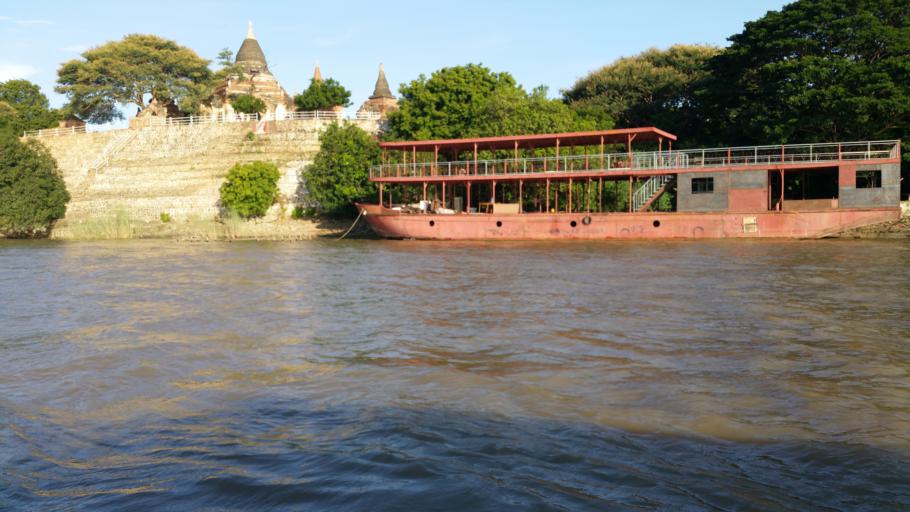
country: MM
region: Magway
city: Pakokku
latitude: 21.1815
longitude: 94.8623
